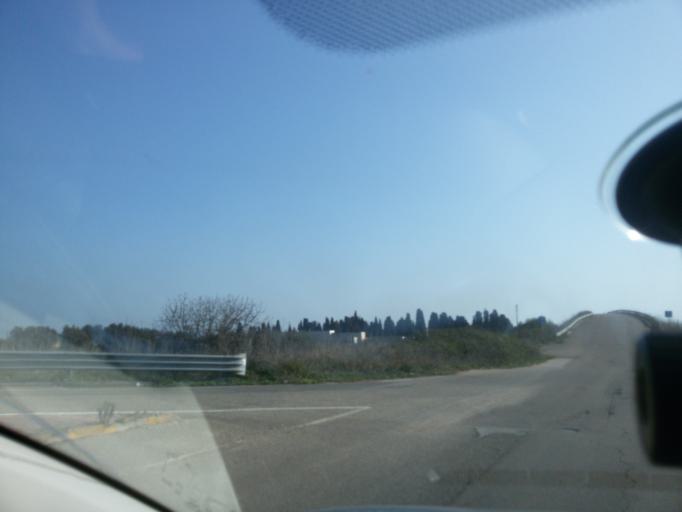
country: IT
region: Apulia
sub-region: Provincia di Brindisi
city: Mesagne
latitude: 40.5701
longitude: 17.8117
